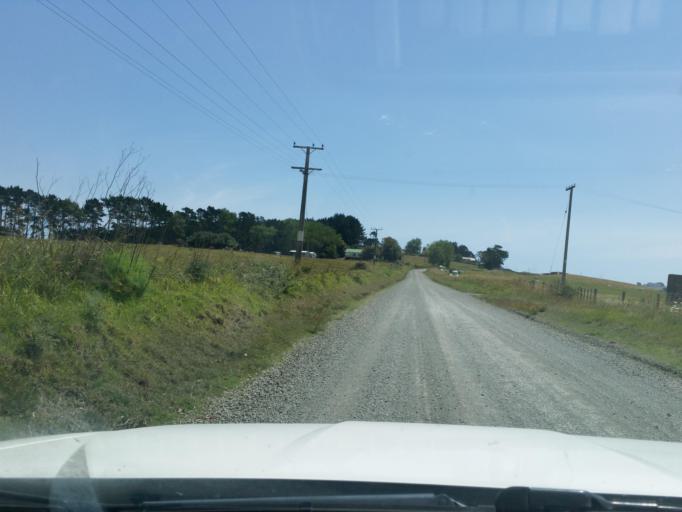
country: NZ
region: Northland
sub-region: Kaipara District
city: Dargaville
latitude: -35.9070
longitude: 173.8007
